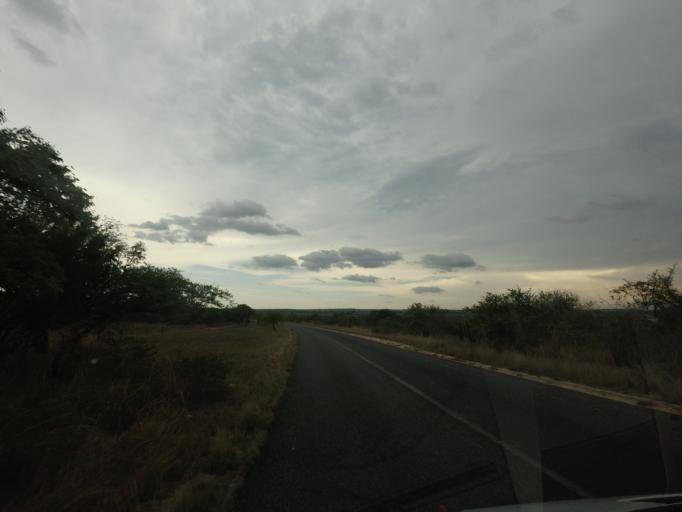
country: ZA
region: Limpopo
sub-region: Mopani District Municipality
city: Hoedspruit
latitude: -24.5356
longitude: 31.0034
